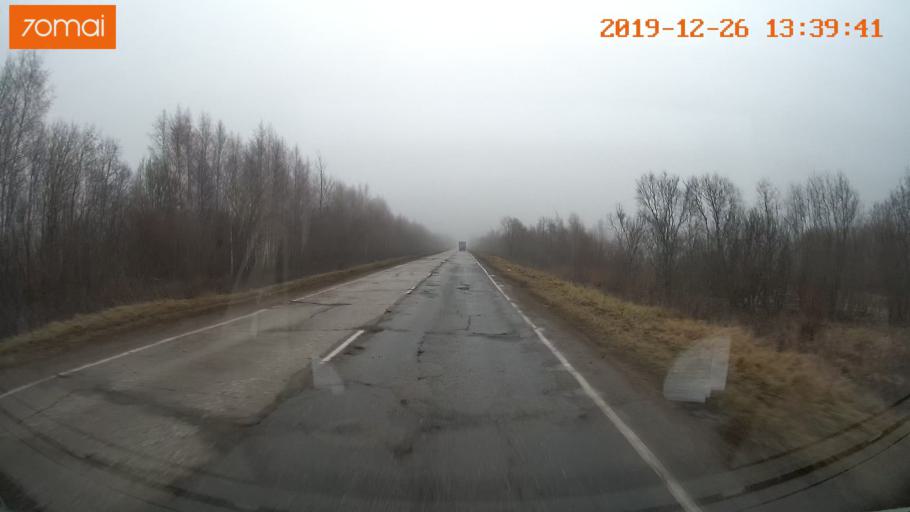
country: RU
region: Vologda
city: Sheksna
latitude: 58.7497
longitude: 38.4158
